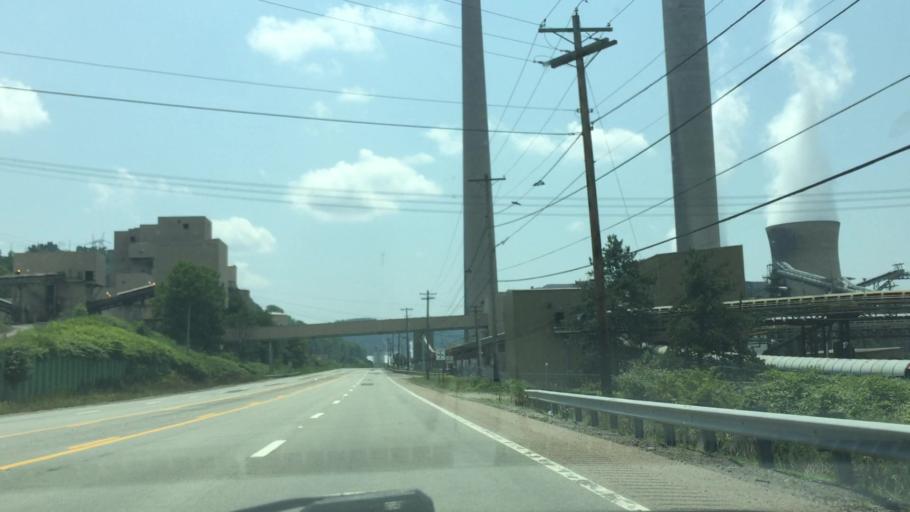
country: US
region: Ohio
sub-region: Belmont County
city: Powhatan Point
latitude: 39.8361
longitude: -80.8155
